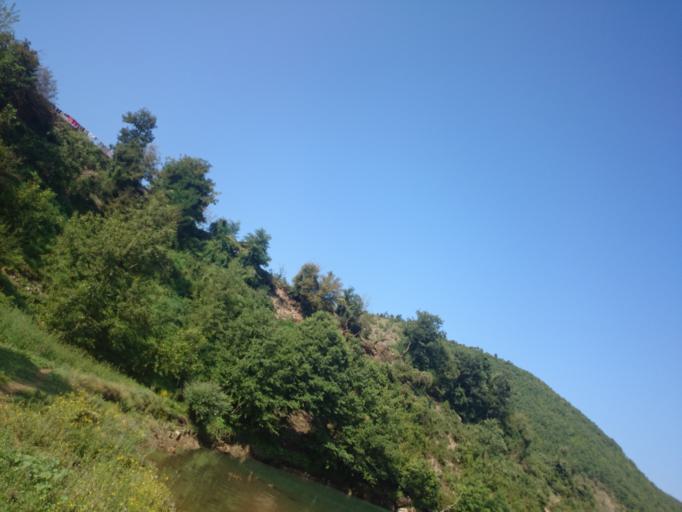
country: AL
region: Diber
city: Peshkopi
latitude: 41.6399
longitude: 20.4054
